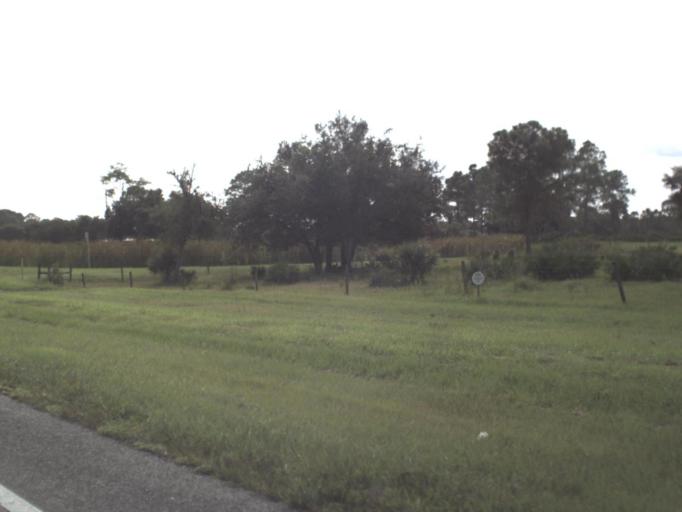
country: US
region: Florida
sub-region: Lee County
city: Alva
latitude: 26.7114
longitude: -81.6433
